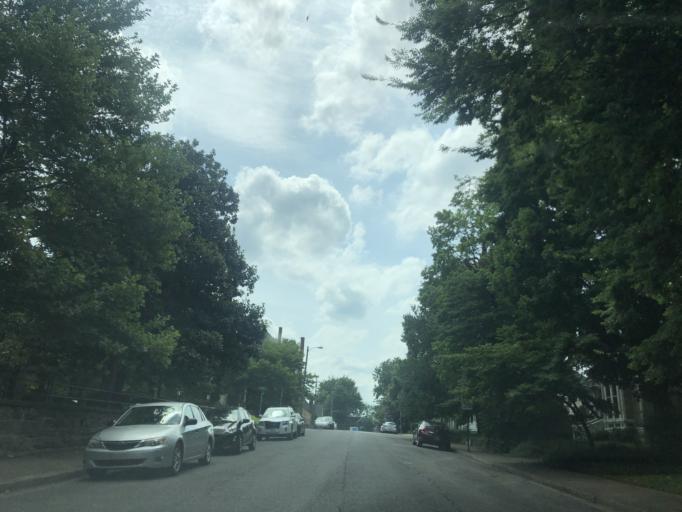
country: US
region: Tennessee
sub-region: Davidson County
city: Nashville
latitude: 36.1760
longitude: -86.7479
